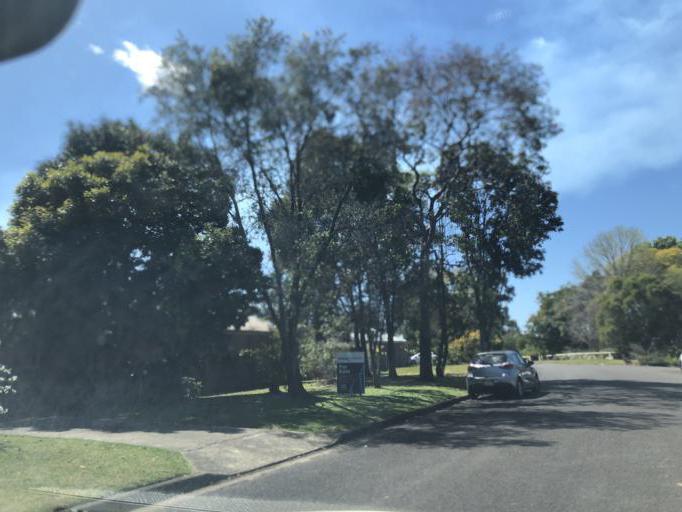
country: AU
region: New South Wales
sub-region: Bellingen
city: Bellingen
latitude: -30.4589
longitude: 152.9045
